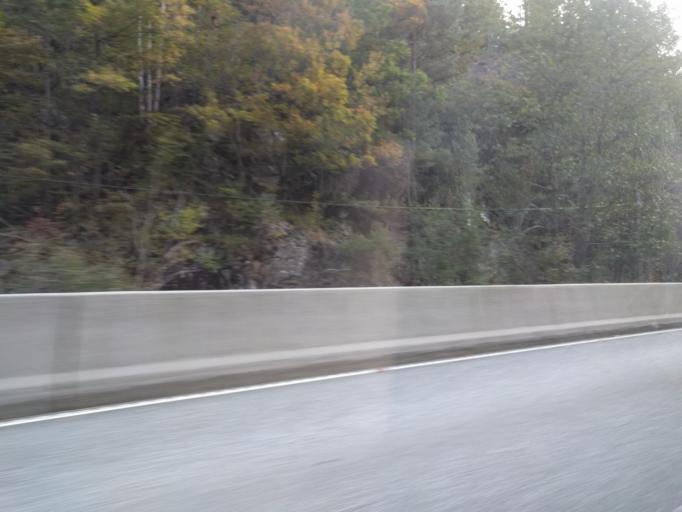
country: NO
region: Vest-Agder
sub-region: Kristiansand
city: Strai
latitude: 58.2449
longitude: 7.8764
